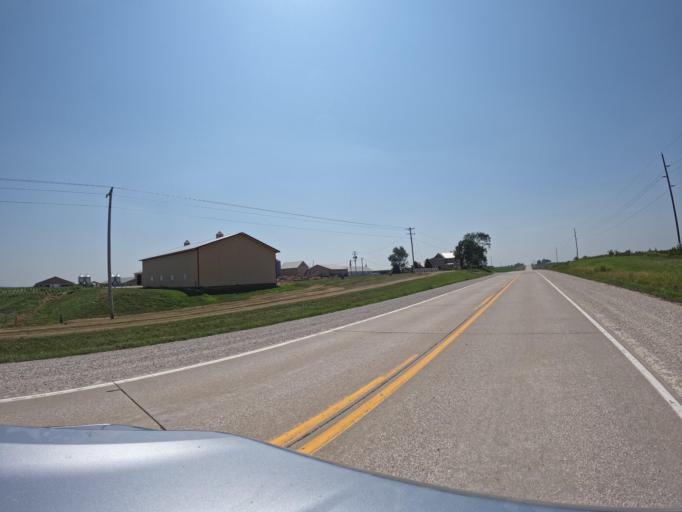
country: US
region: Iowa
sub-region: Keokuk County
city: Sigourney
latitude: 41.3368
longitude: -92.2504
